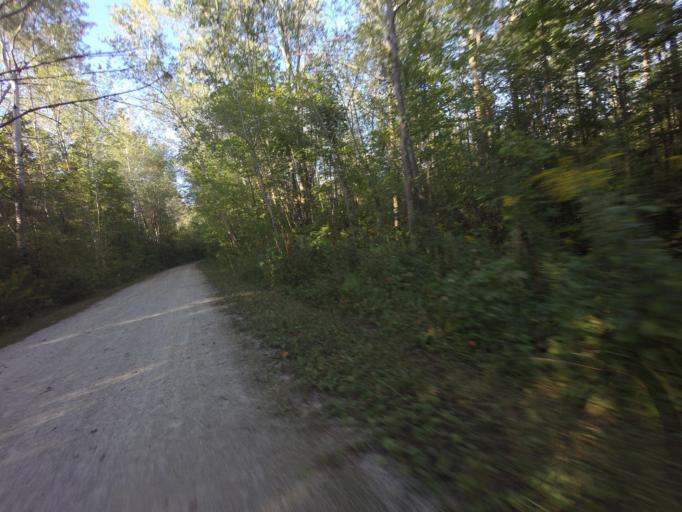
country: CA
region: Ontario
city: Orangeville
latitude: 43.8099
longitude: -79.9322
